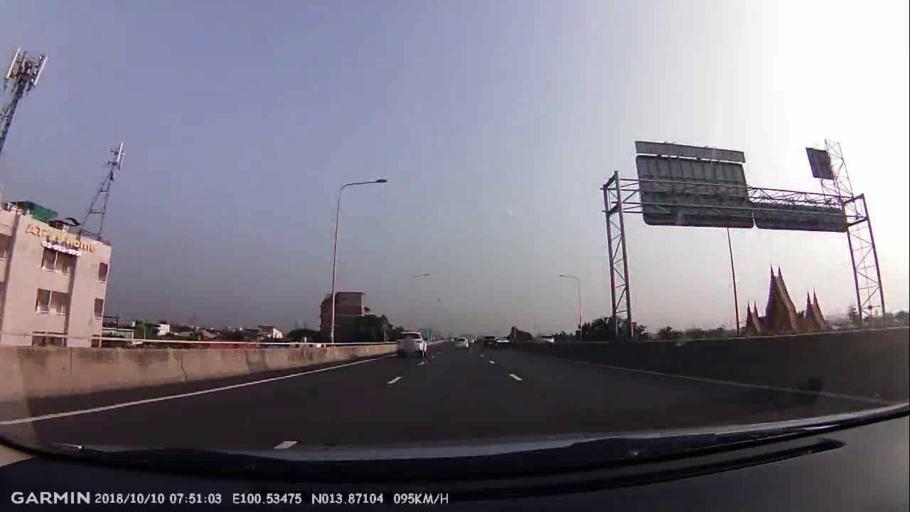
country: TH
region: Nonthaburi
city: Mueang Nonthaburi
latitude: 13.8714
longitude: 100.5340
